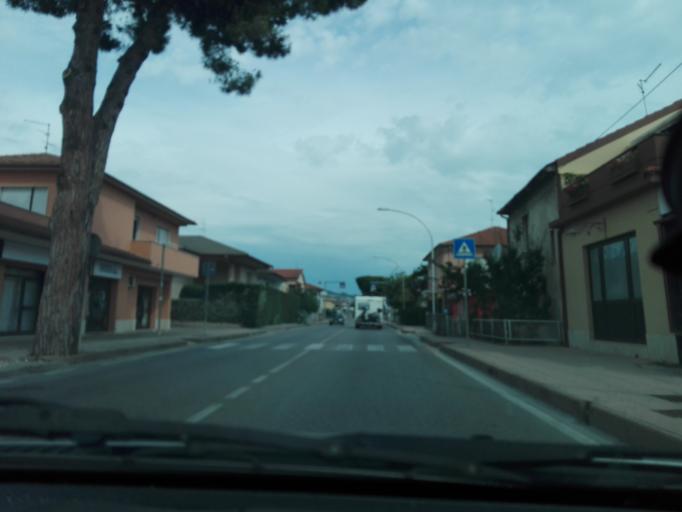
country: IT
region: Abruzzo
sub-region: Provincia di Pescara
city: San Martino Bassa
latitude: 42.5265
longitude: 14.1378
